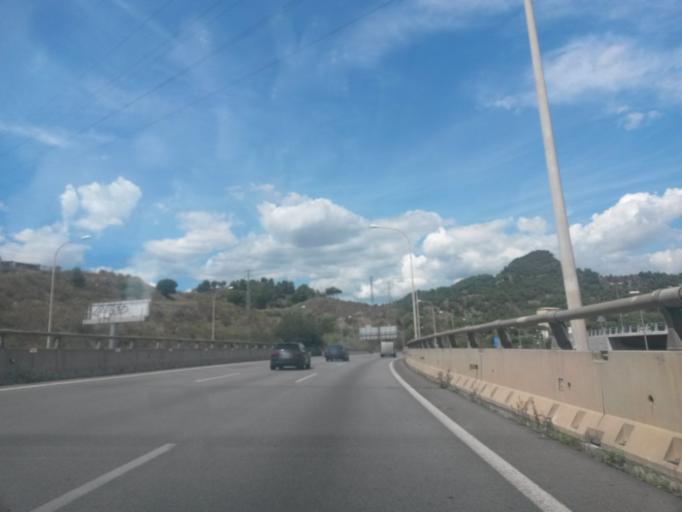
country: ES
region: Catalonia
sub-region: Provincia de Barcelona
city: Montcada i Reixac
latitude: 41.4661
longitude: 2.1780
